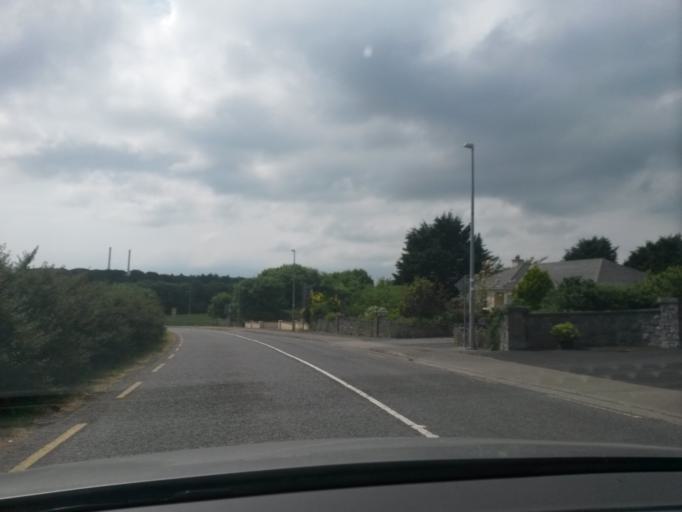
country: IE
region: Munster
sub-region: An Clar
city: Kilrush
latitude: 52.6172
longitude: -9.3832
